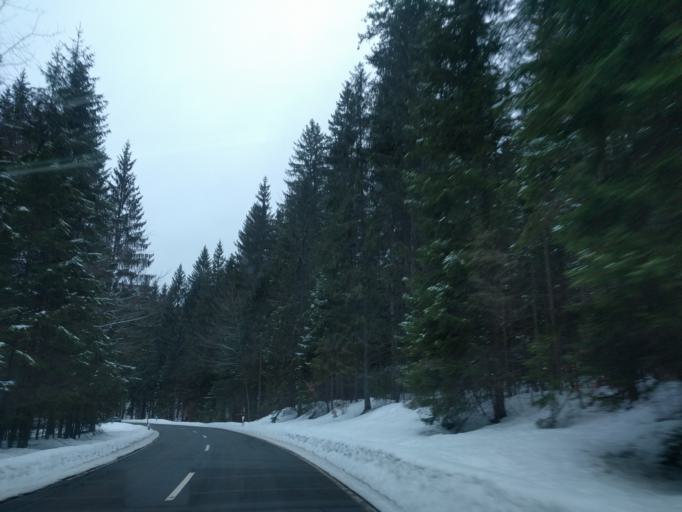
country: DE
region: Bavaria
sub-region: Lower Bavaria
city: Lindberg
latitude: 49.0533
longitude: 13.2928
